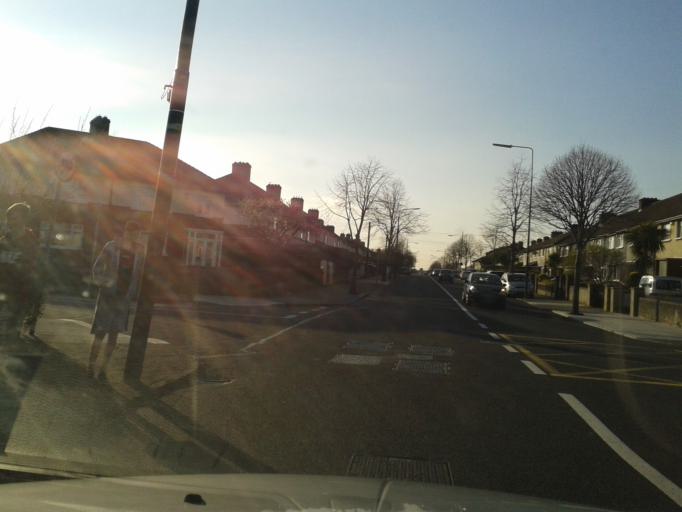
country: IE
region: Leinster
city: Beaumont
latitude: 53.3832
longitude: -6.2467
